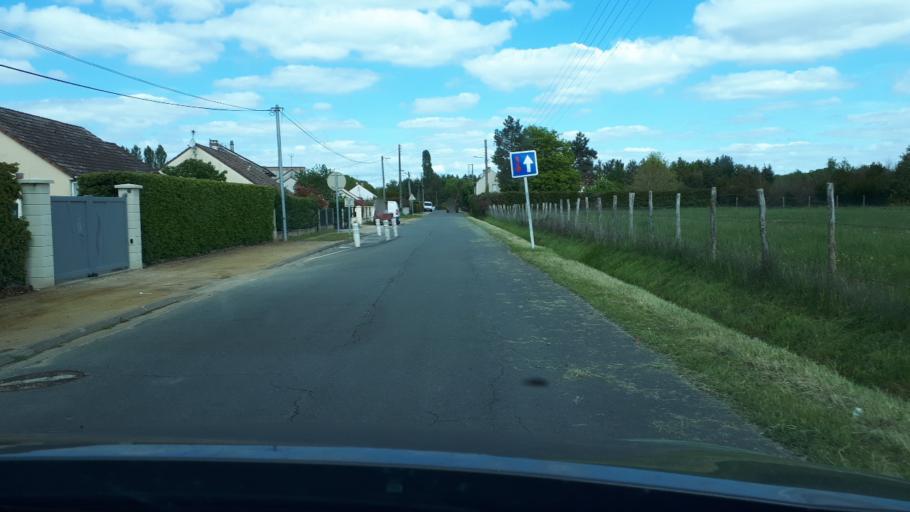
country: FR
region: Centre
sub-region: Departement du Loir-et-Cher
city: Saint-Viatre
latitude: 47.5236
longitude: 1.9276
